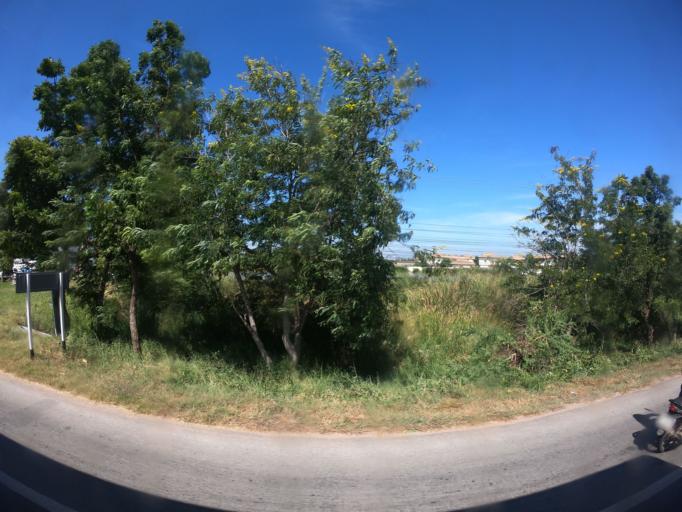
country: TH
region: Nakhon Ratchasima
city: Nakhon Ratchasima
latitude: 15.0387
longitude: 102.1468
